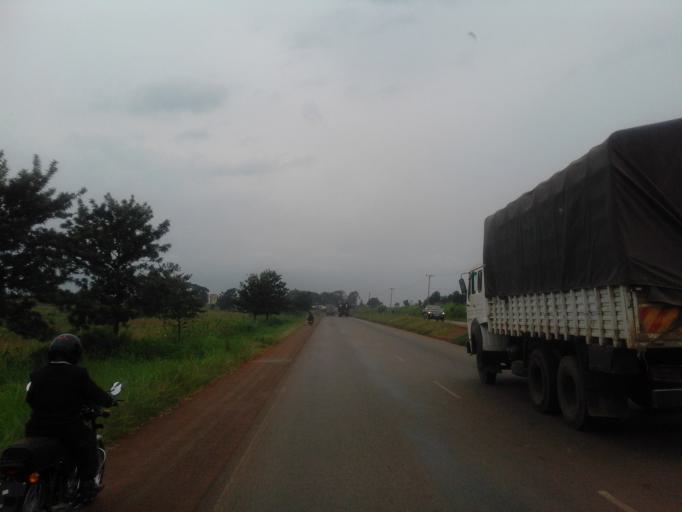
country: UG
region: Eastern Region
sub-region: Jinja District
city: Jinja
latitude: 0.4435
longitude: 33.2074
